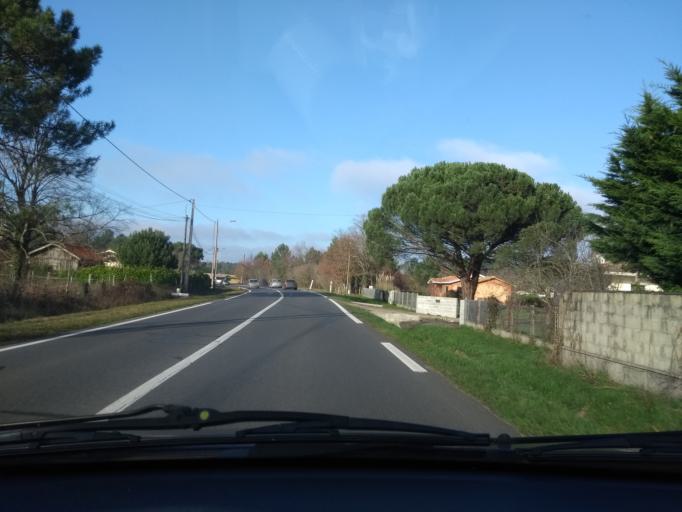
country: FR
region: Aquitaine
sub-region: Departement de la Gironde
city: Mios
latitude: 44.6222
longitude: -0.9519
